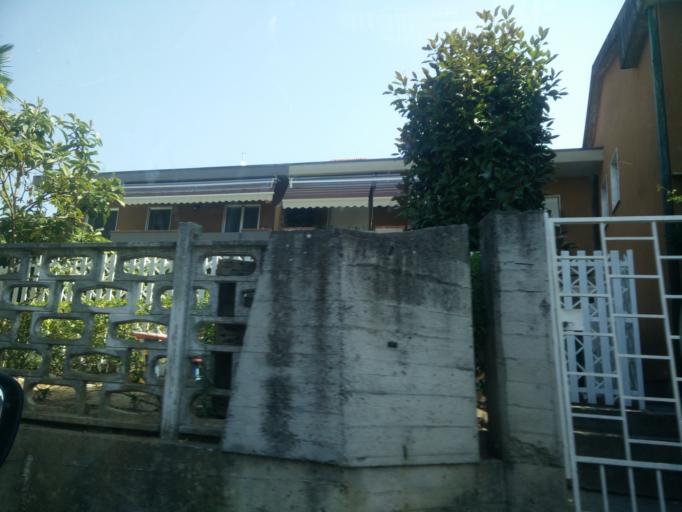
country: IT
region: Tuscany
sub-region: Provincia di Massa-Carrara
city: Carrara
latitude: 44.0585
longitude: 10.0829
